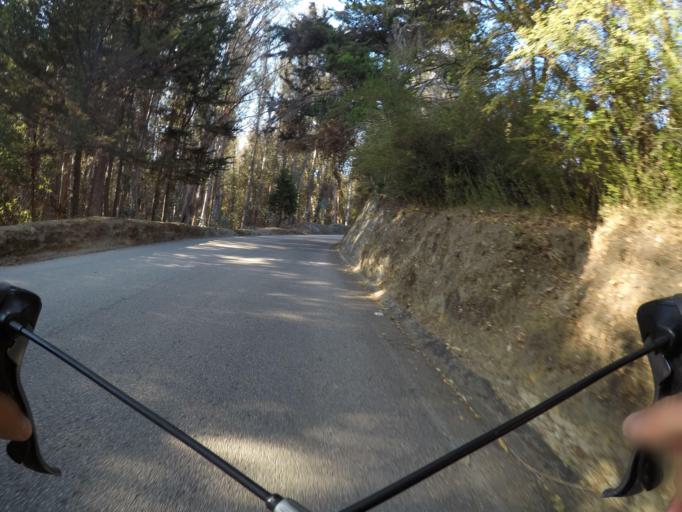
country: US
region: California
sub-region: Santa Cruz County
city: Live Oak
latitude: 36.9945
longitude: -121.9842
